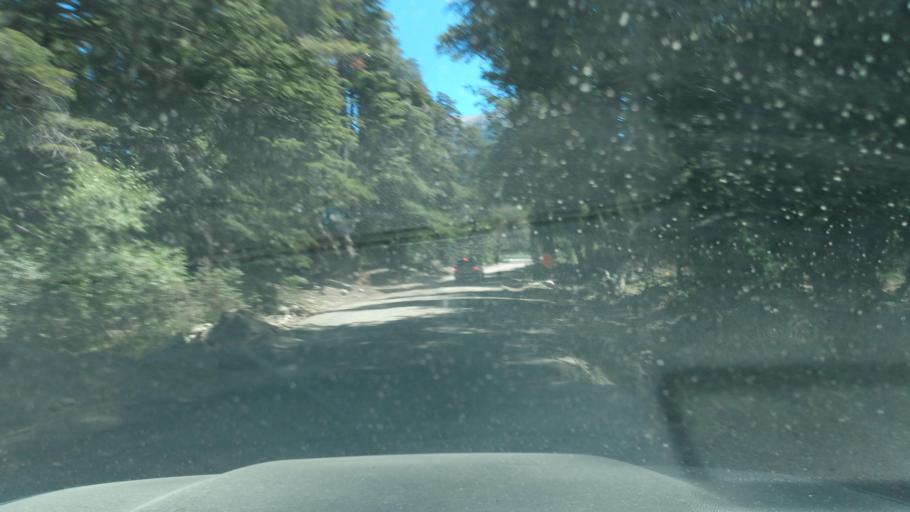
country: AR
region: Neuquen
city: Villa La Angostura
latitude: -40.6286
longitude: -71.4848
